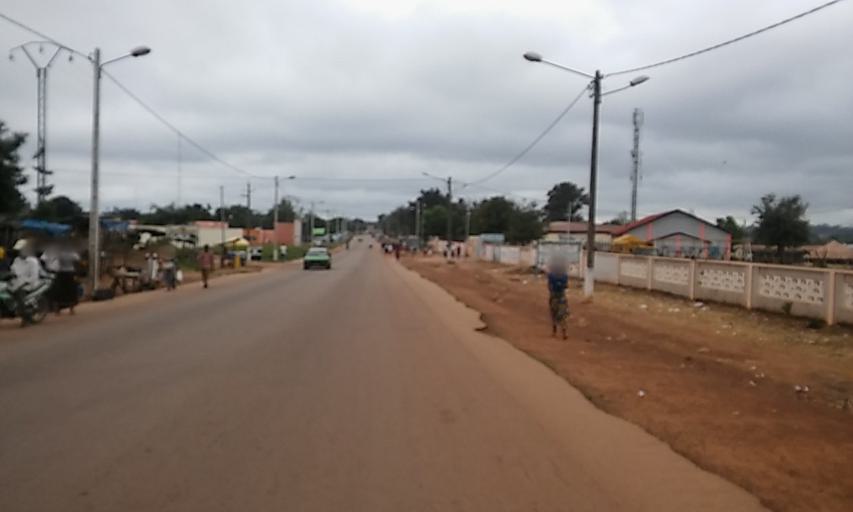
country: CI
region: Dix-Huit Montagnes
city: Duekoue
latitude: 6.7396
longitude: -7.3433
